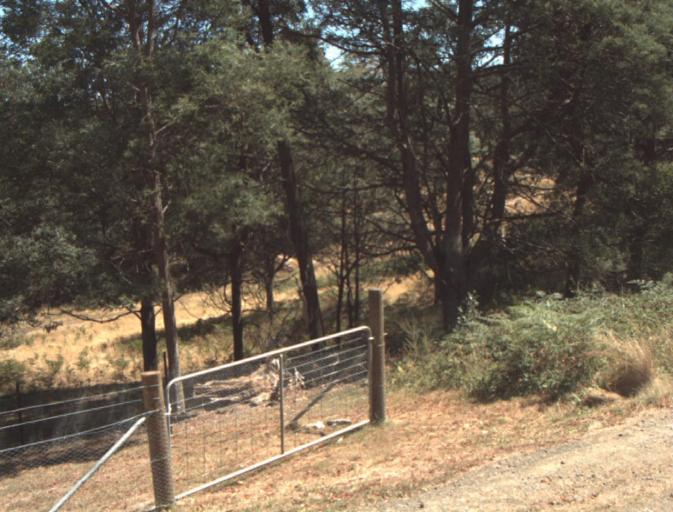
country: AU
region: Tasmania
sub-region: Launceston
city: Newstead
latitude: -41.3518
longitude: 147.3789
